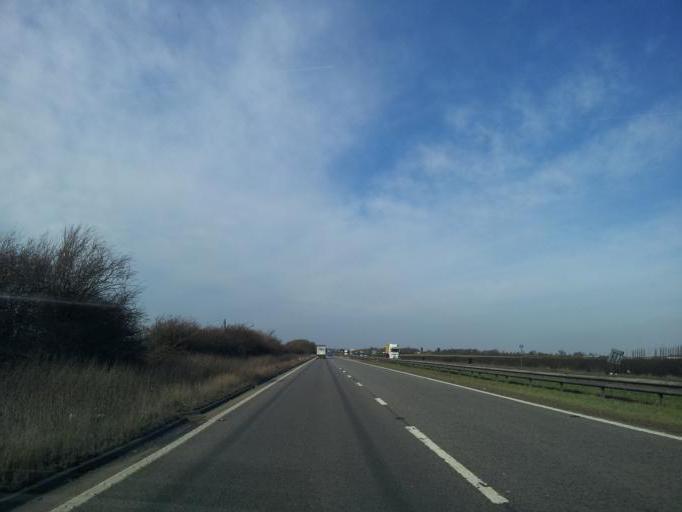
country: GB
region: England
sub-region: Lincolnshire
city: Long Bennington
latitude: 53.0232
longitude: -0.7681
